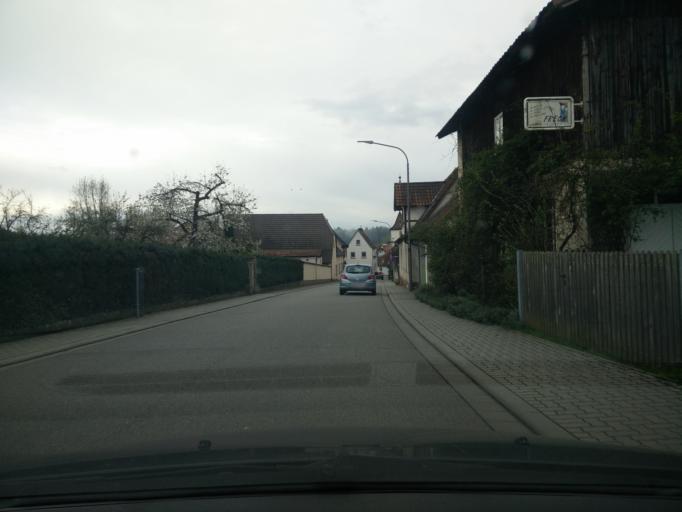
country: DE
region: Rheinland-Pfalz
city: Vollmersweiler
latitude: 49.0601
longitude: 8.0807
